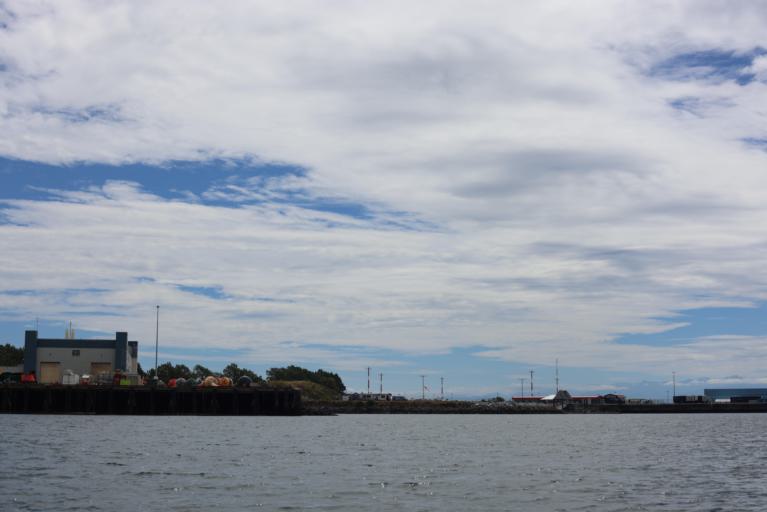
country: CA
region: British Columbia
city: Victoria
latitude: 48.4222
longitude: -123.3911
